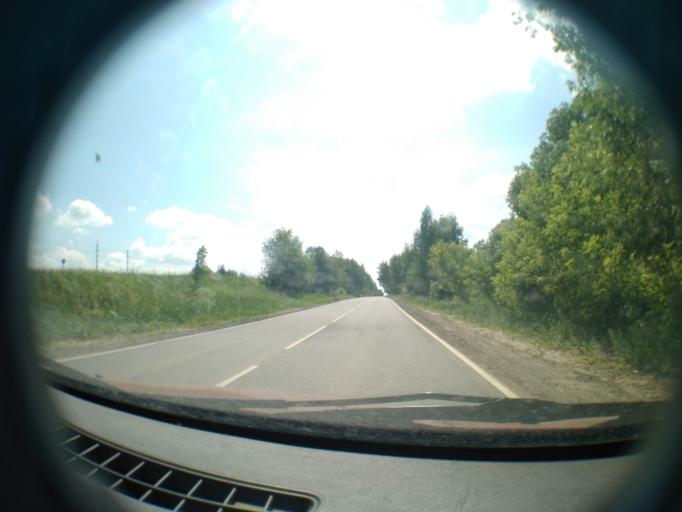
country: RU
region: Moskovskaya
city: Ostrovtsy
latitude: 55.5289
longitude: 38.0007
